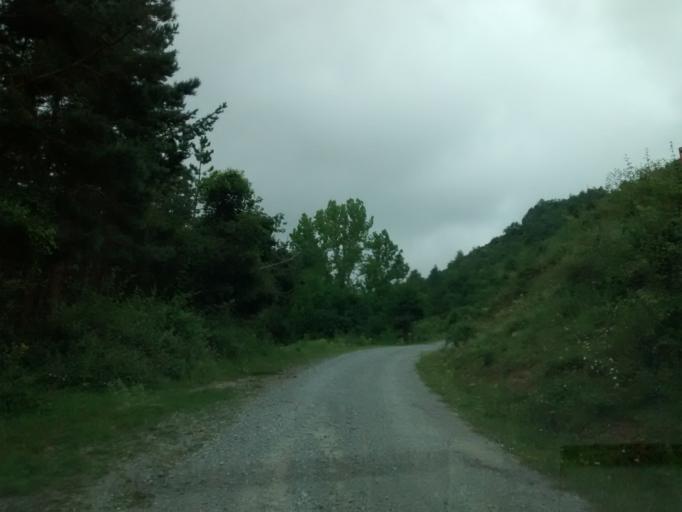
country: ES
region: La Rioja
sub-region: Provincia de La Rioja
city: Ajamil
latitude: 42.1620
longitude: -2.4856
